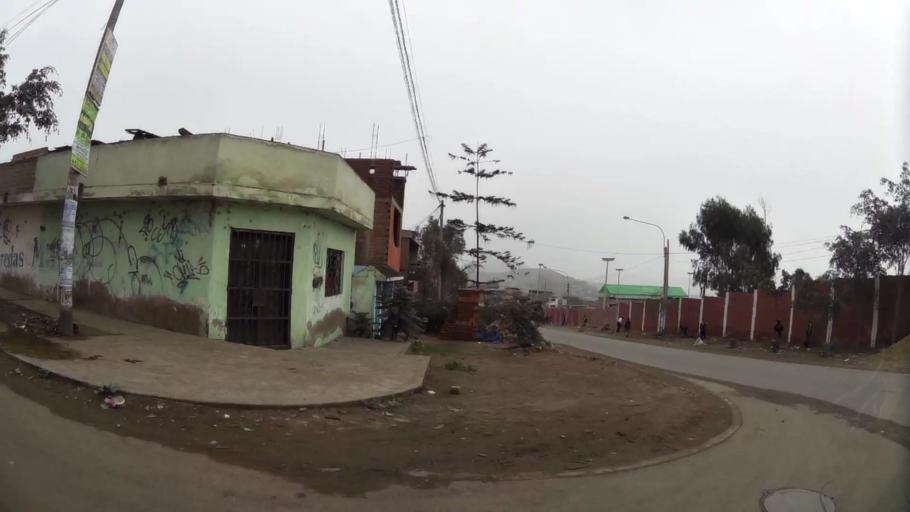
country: PE
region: Lima
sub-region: Lima
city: Surco
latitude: -12.1862
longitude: -76.9287
